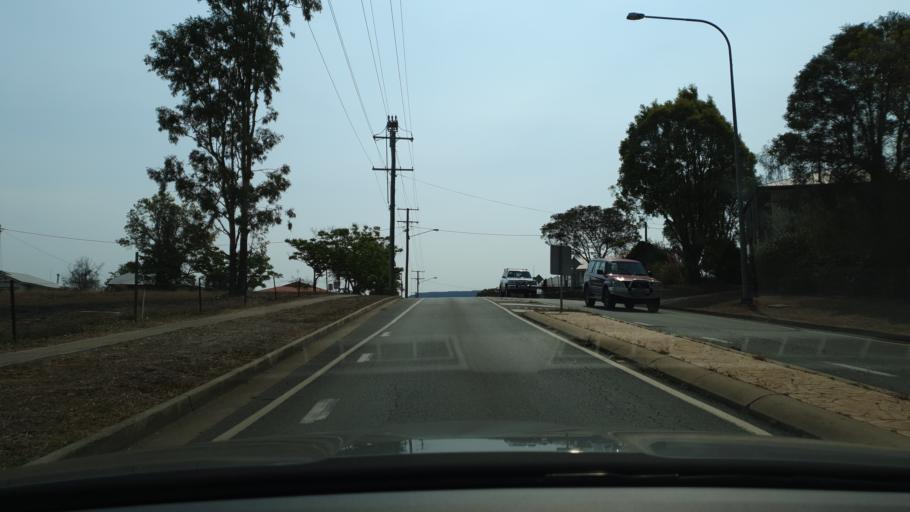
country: AU
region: Queensland
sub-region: Ipswich
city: Deebing Heights
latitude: -27.9922
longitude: 152.6887
